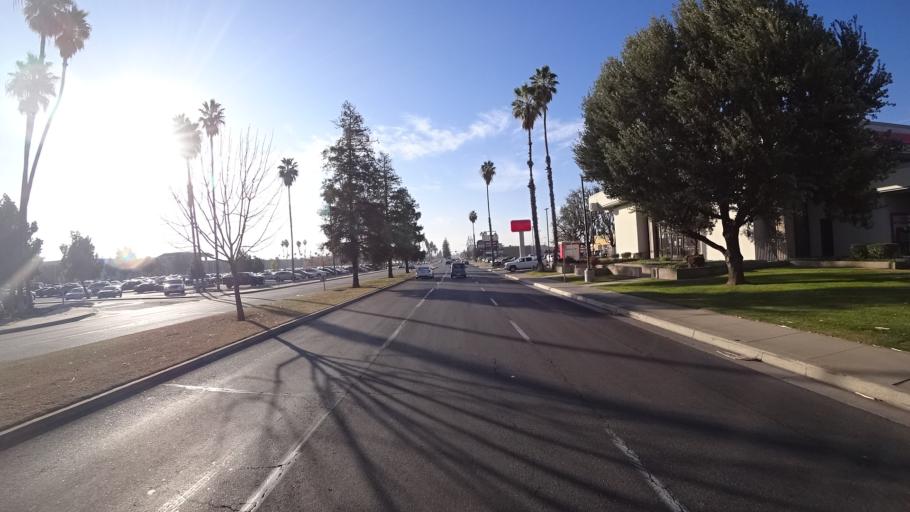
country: US
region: California
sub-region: Kern County
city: Bakersfield
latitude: 35.3395
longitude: -119.0322
